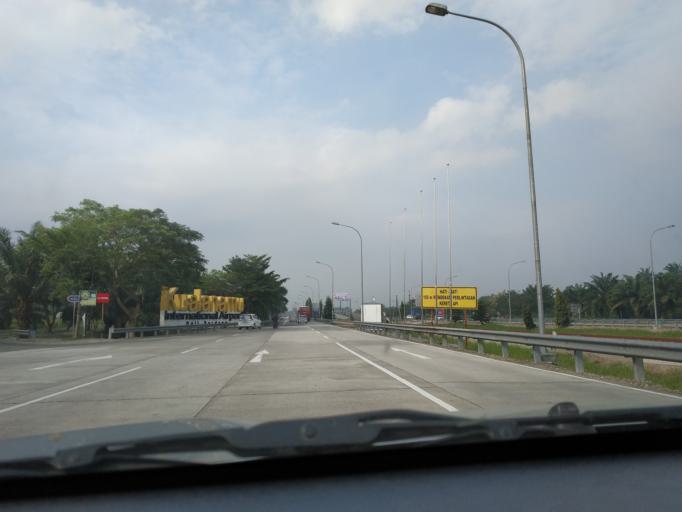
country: ID
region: North Sumatra
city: Percut
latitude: 3.6136
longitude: 98.8575
